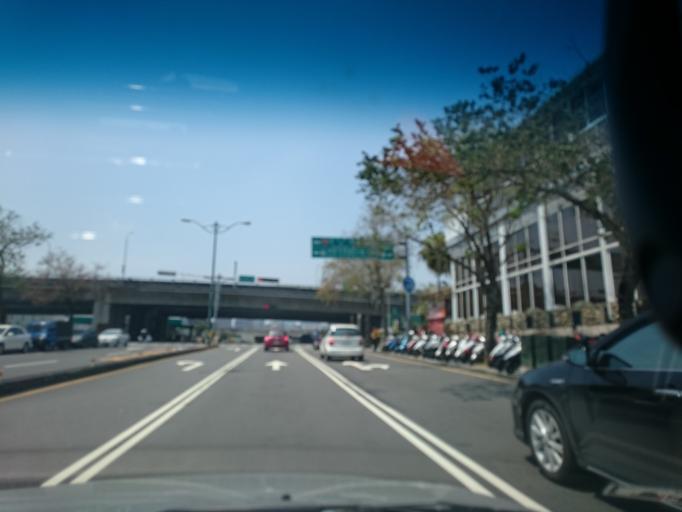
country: TW
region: Taiwan
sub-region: Taichung City
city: Taichung
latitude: 24.1795
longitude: 120.6358
